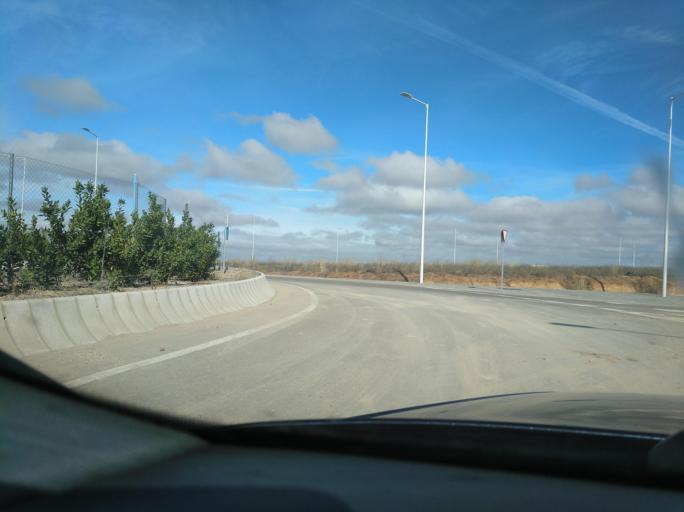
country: ES
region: Extremadura
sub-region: Provincia de Badajoz
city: Badajoz
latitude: 38.9106
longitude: -7.0109
